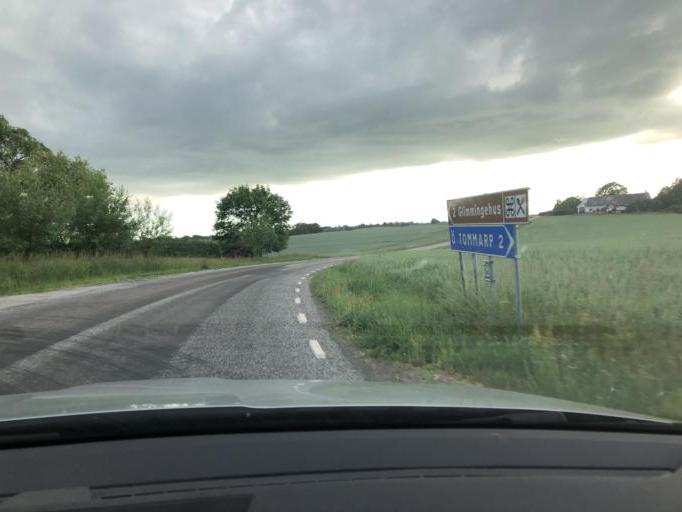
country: SE
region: Skane
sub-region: Simrishamns Kommun
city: Simrishamn
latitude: 55.5126
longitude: 14.2377
